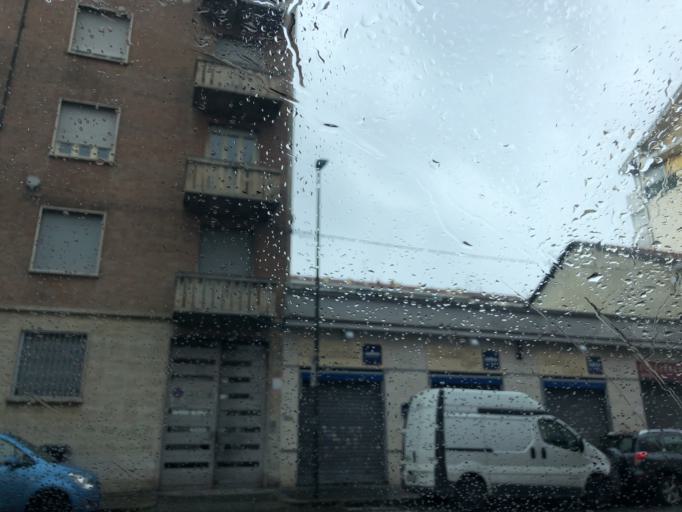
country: IT
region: Piedmont
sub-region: Provincia di Torino
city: Lesna
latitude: 45.0790
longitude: 7.6305
